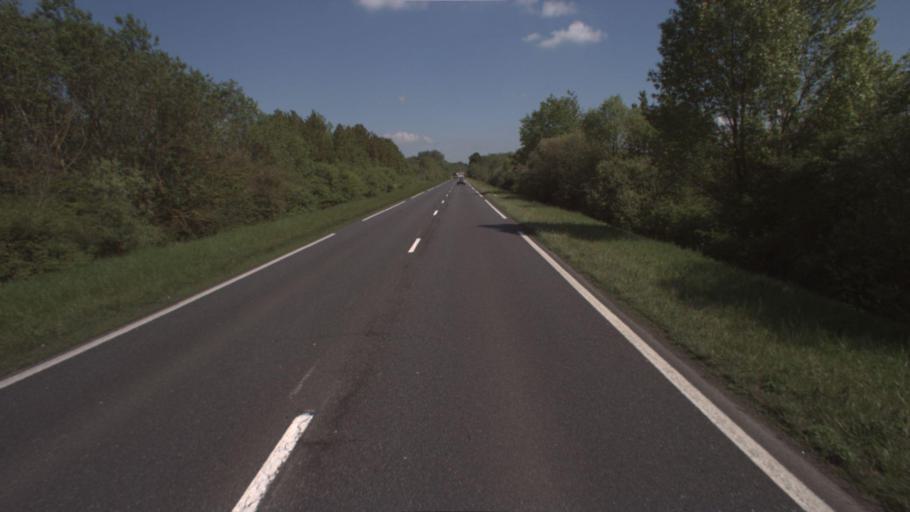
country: FR
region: Ile-de-France
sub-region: Departement de Seine-et-Marne
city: Chaumes-en-Brie
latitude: 48.6778
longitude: 2.8138
